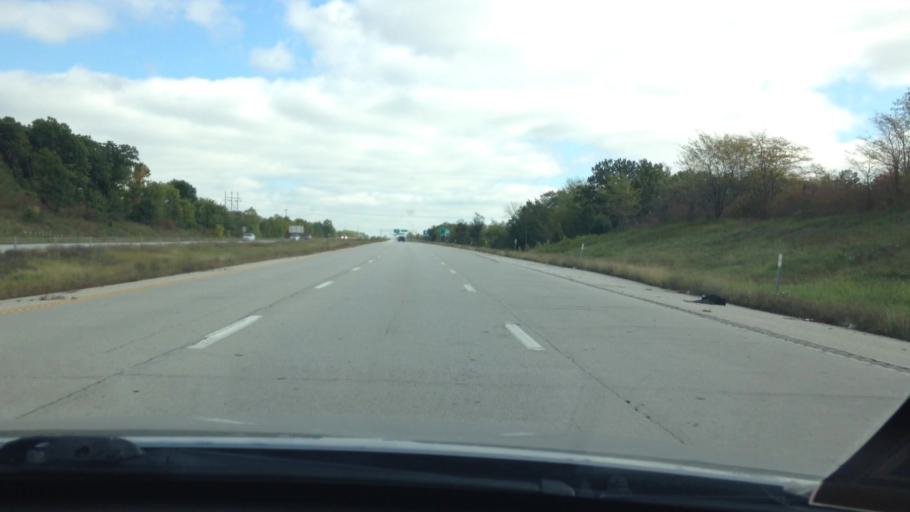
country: US
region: Missouri
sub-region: Platte County
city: Weatherby Lake
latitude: 39.2538
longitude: -94.6807
